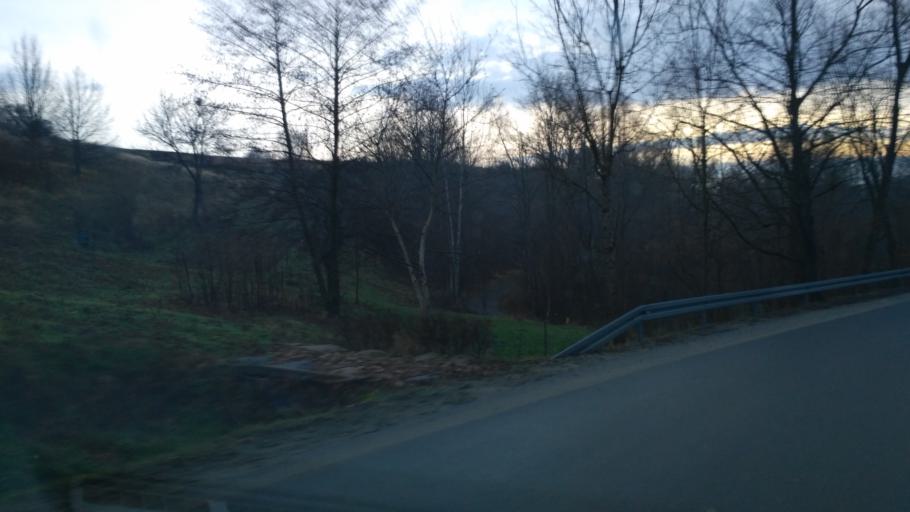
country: PL
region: Subcarpathian Voivodeship
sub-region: Powiat strzyzowski
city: Jawornik
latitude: 49.8746
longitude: 21.8657
